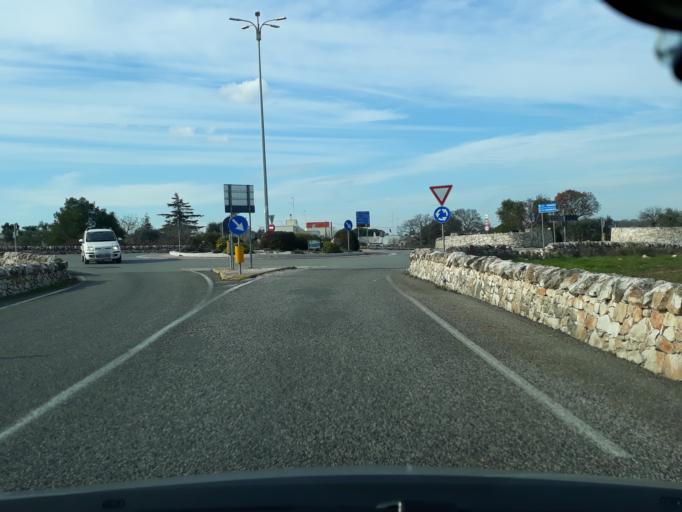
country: IT
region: Apulia
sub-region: Provincia di Bari
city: Locorotondo
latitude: 40.7615
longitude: 17.3334
